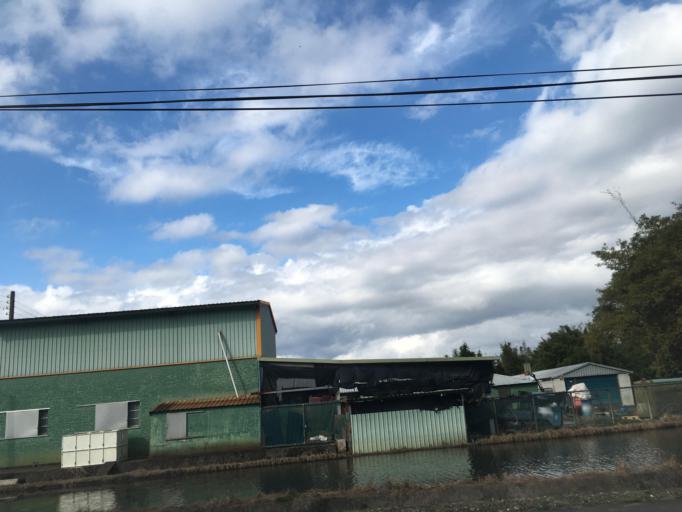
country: TW
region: Taiwan
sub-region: Yilan
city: Yilan
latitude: 24.6863
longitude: 121.7156
